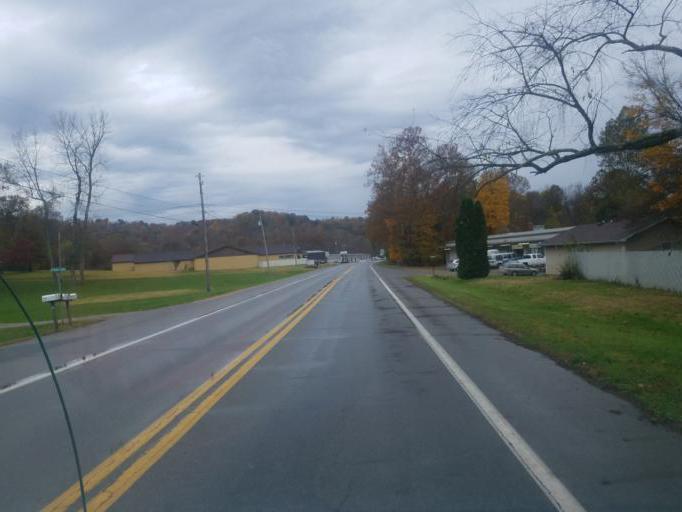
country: US
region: West Virginia
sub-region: Wood County
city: Boaz
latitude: 39.3650
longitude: -81.4882
